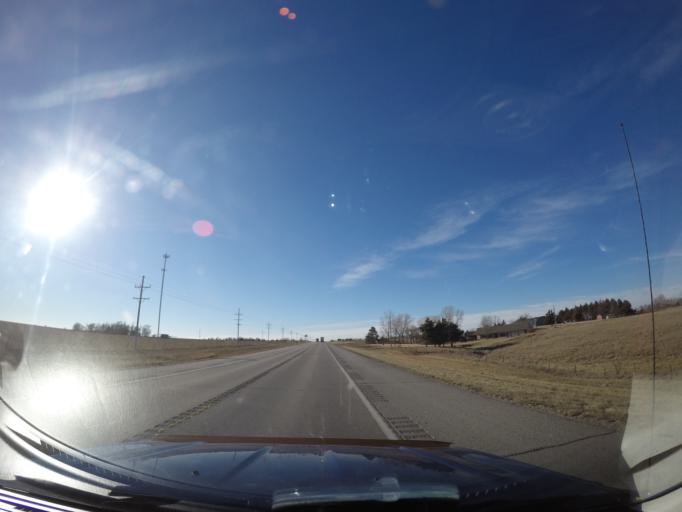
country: US
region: Kansas
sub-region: Marion County
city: Hillsboro
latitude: 38.3627
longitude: -97.2347
